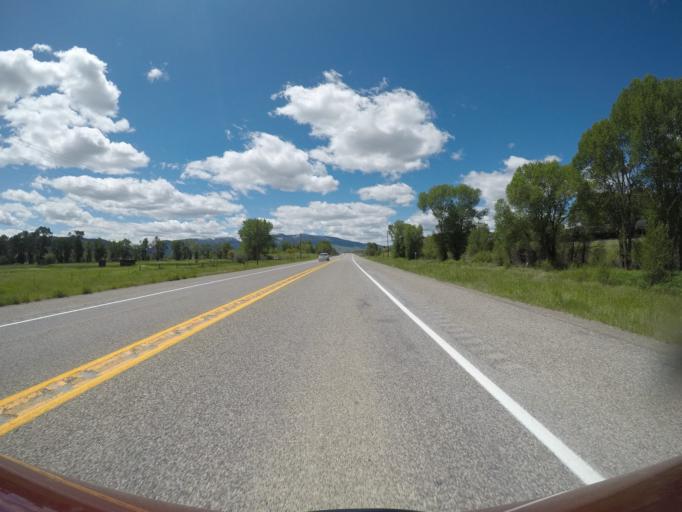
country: US
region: Montana
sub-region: Park County
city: Livingston
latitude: 45.6770
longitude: -110.5314
